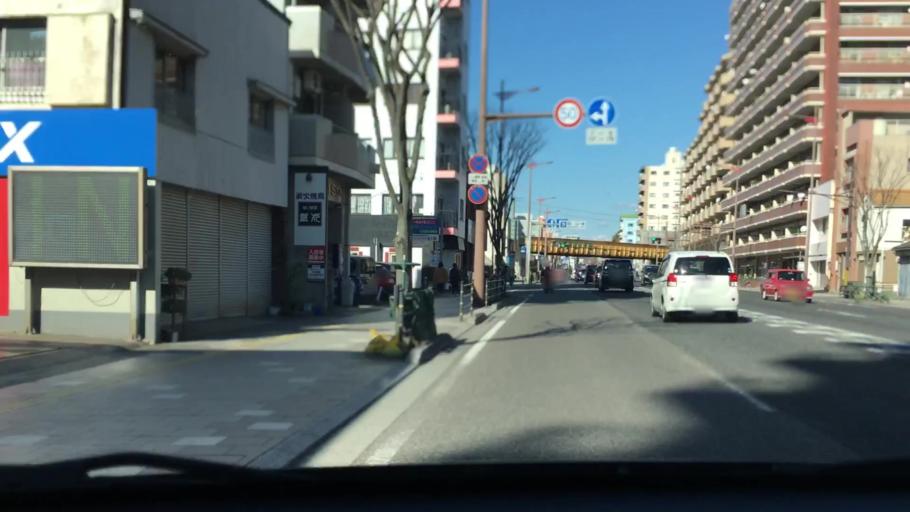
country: JP
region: Kagoshima
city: Kagoshima-shi
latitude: 31.5918
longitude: 130.5448
